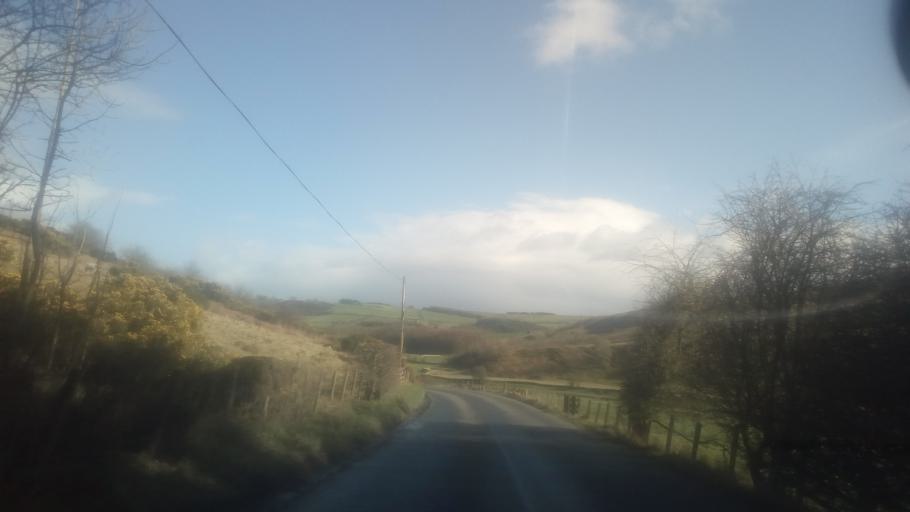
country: GB
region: Scotland
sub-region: The Scottish Borders
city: Hawick
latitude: 55.4130
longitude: -2.8485
